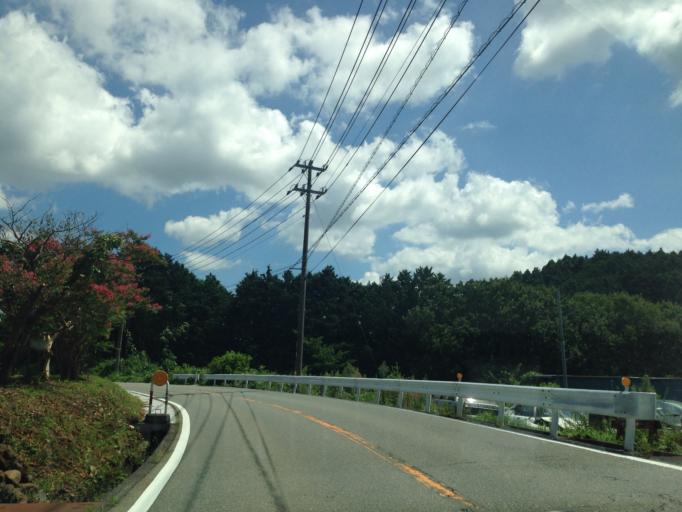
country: JP
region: Shizuoka
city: Gotemba
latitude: 35.2266
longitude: 138.8799
